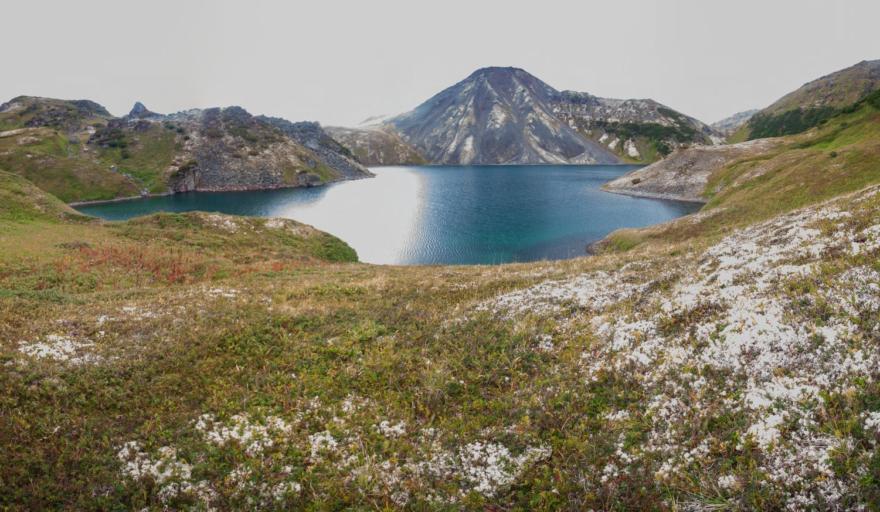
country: RU
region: Kamtsjatka
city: Yelizovo
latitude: 53.8805
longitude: 158.0293
